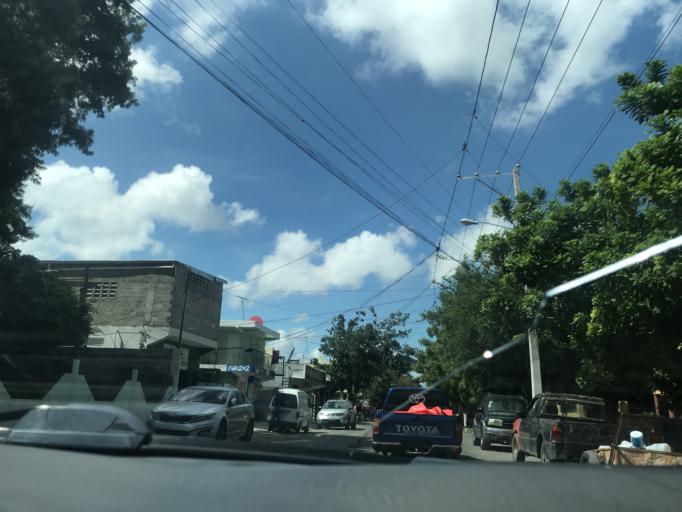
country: DO
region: Santiago
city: Palmar Arriba
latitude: 19.4929
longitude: -70.7411
